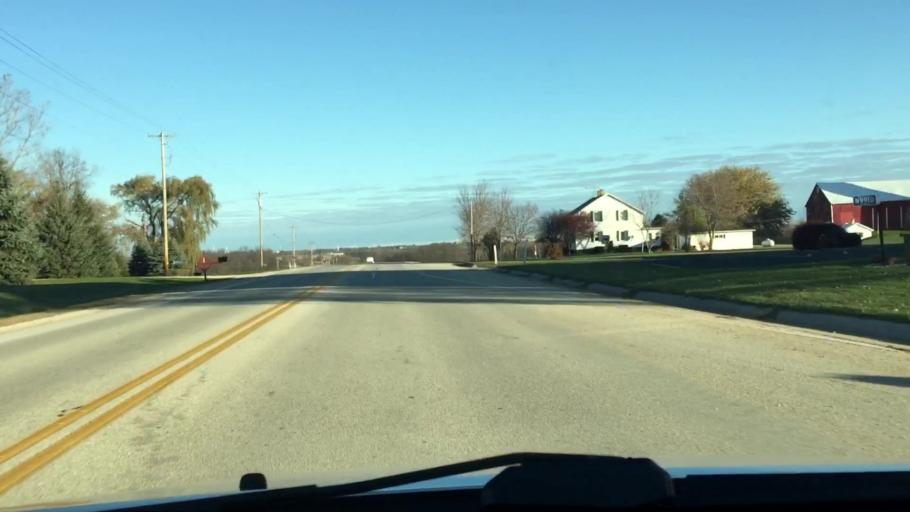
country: US
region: Wisconsin
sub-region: Dodge County
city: Theresa
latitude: 43.5512
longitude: -88.4435
